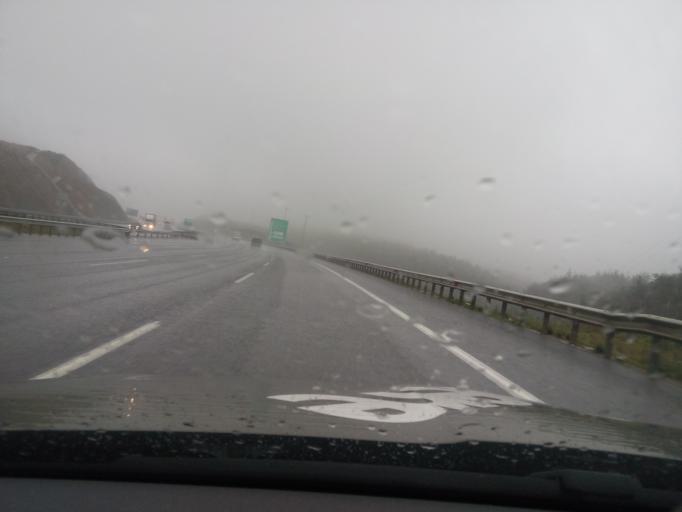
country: TR
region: Istanbul
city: Basaksehir
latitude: 41.1512
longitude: 28.8064
